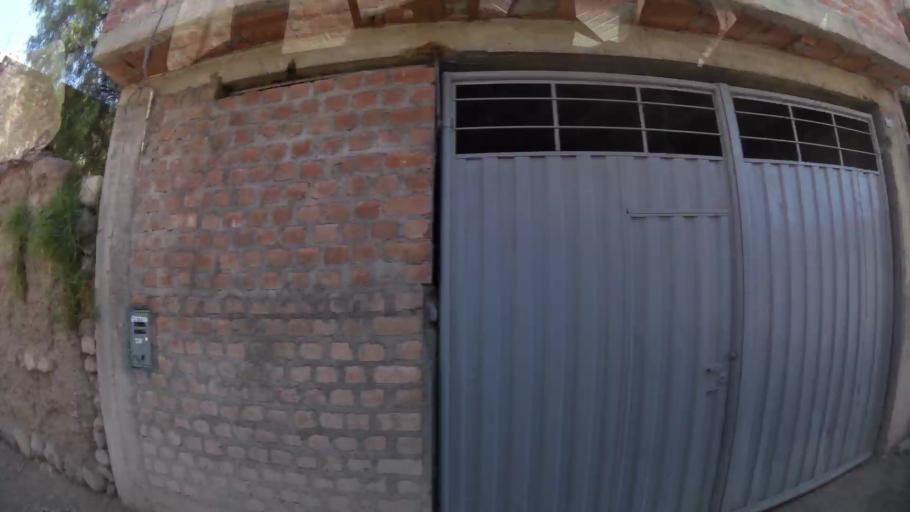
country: PE
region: Ayacucho
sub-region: Provincia de Huamanga
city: Ayacucho
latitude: -13.1660
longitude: -74.2313
